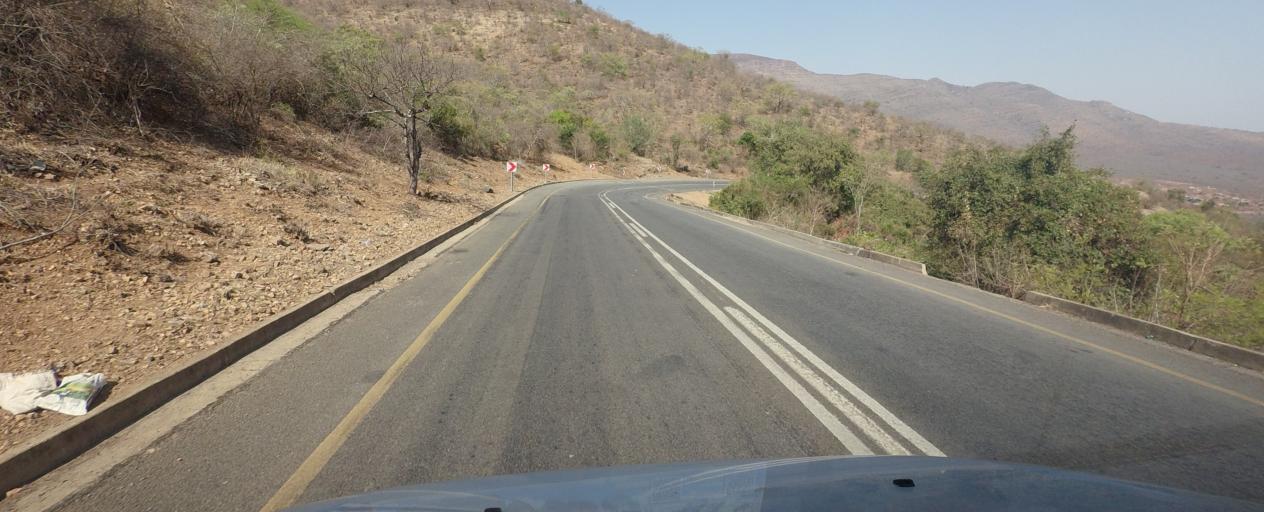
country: ZA
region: Mpumalanga
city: Burgersfort
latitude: -24.4759
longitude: 30.6200
